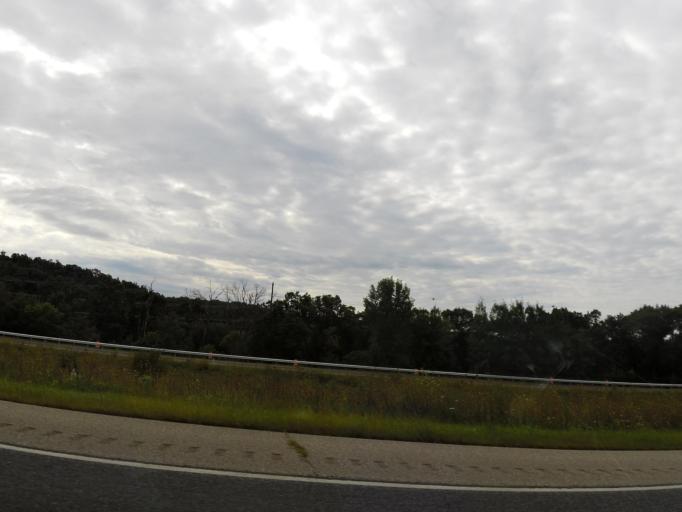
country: US
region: Wisconsin
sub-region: Monroe County
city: Tomah
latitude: 43.9392
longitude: -90.6132
